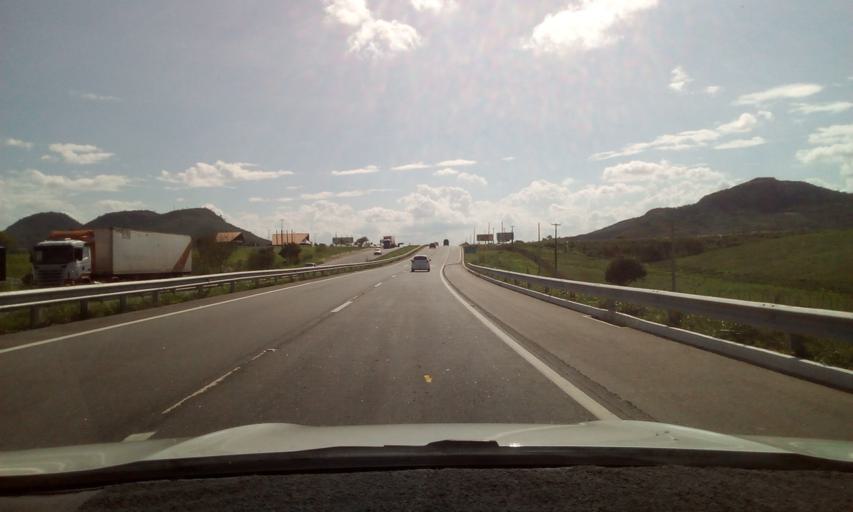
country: BR
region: Paraiba
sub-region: Gurinhem
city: Gurinhem
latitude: -7.1703
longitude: -35.3805
